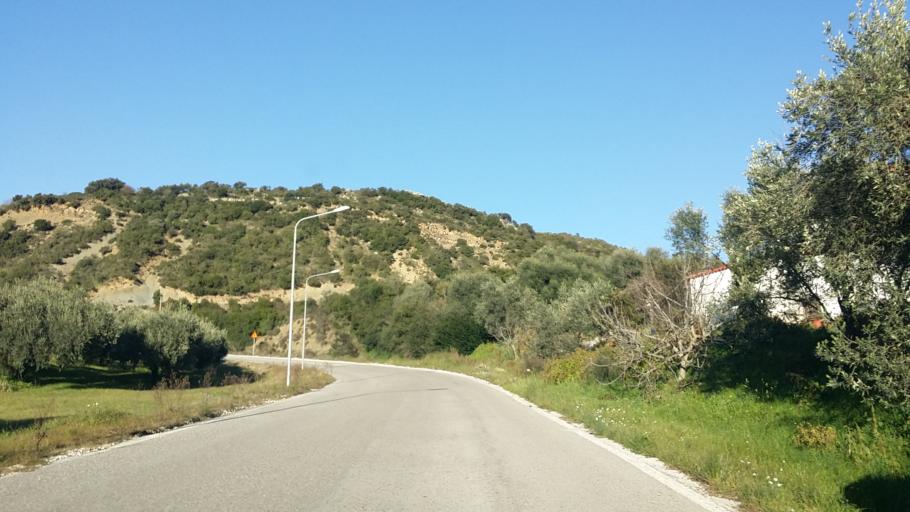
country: GR
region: West Greece
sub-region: Nomos Aitolias kai Akarnanias
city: Sardinia
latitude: 38.8738
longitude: 21.2573
